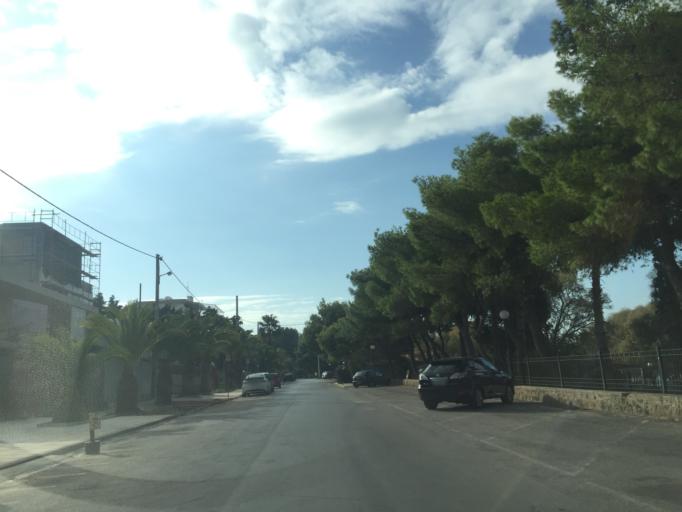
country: GR
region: Attica
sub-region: Nomarchia Anatolikis Attikis
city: Vouliagmeni
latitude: 37.8270
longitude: 23.7707
